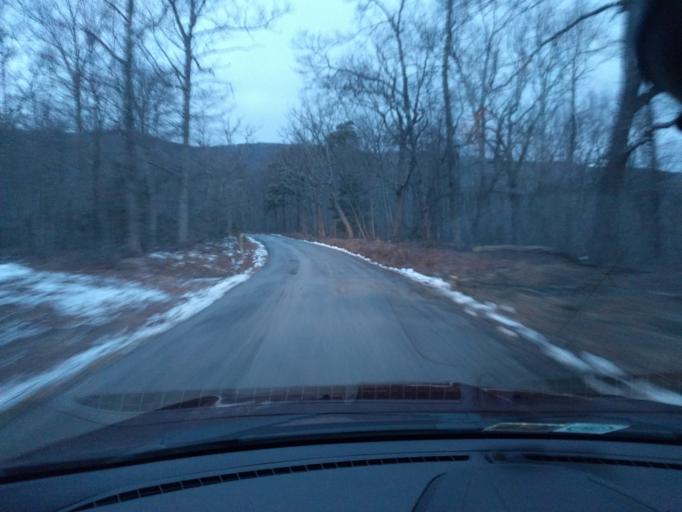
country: US
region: Virginia
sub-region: Alleghany County
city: Clifton Forge
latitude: 37.8627
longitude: -79.8773
